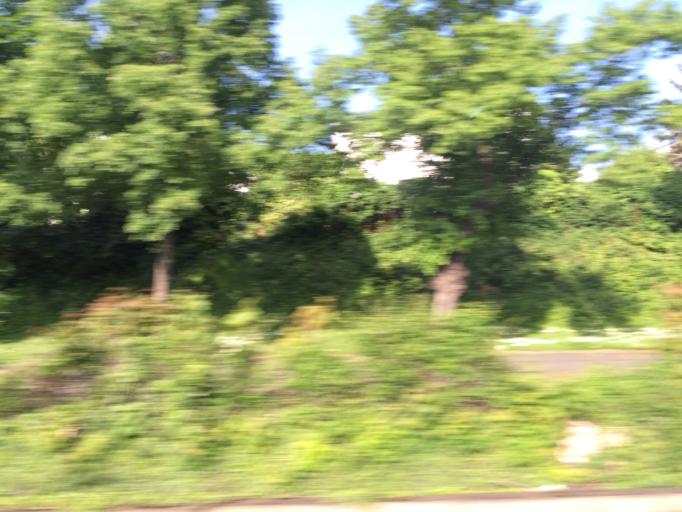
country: DE
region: North Rhine-Westphalia
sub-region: Regierungsbezirk Koln
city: Konigswinter
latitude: 50.7137
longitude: 7.1606
